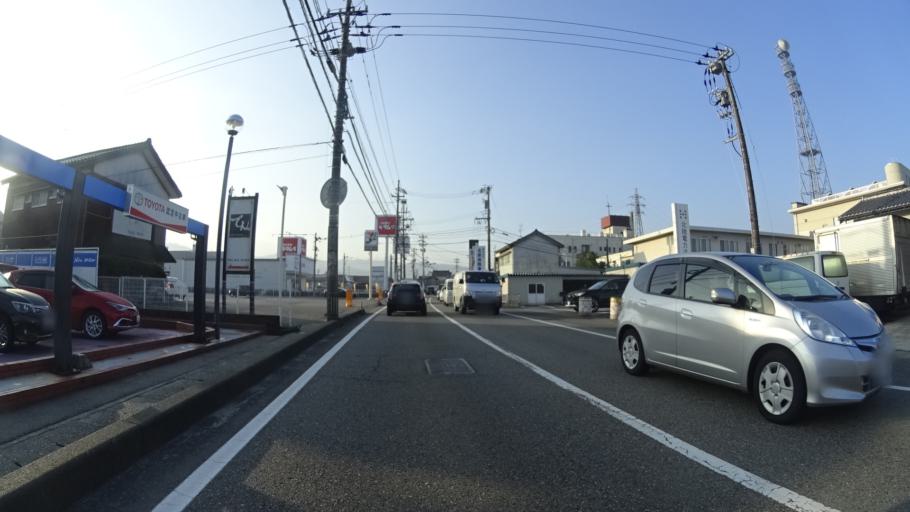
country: JP
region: Ishikawa
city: Nanao
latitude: 37.0354
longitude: 136.9687
